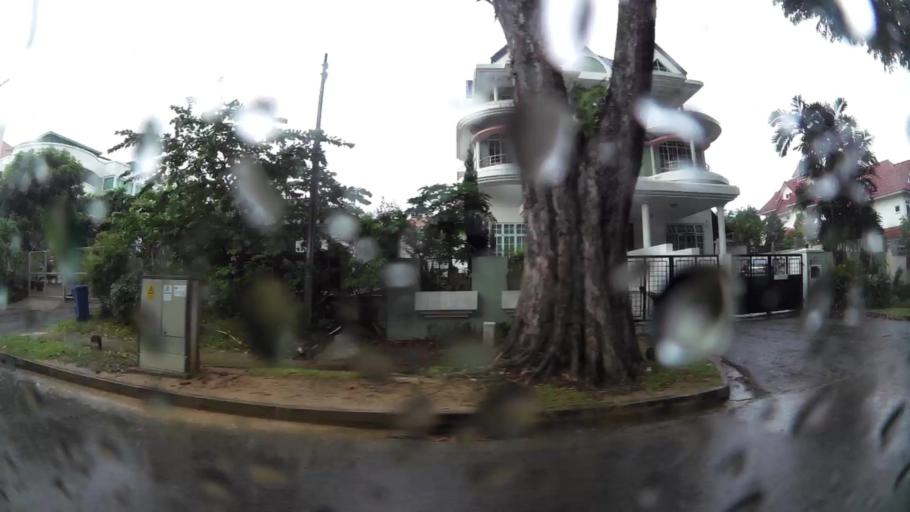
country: SG
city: Singapore
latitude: 1.3361
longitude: 103.9547
